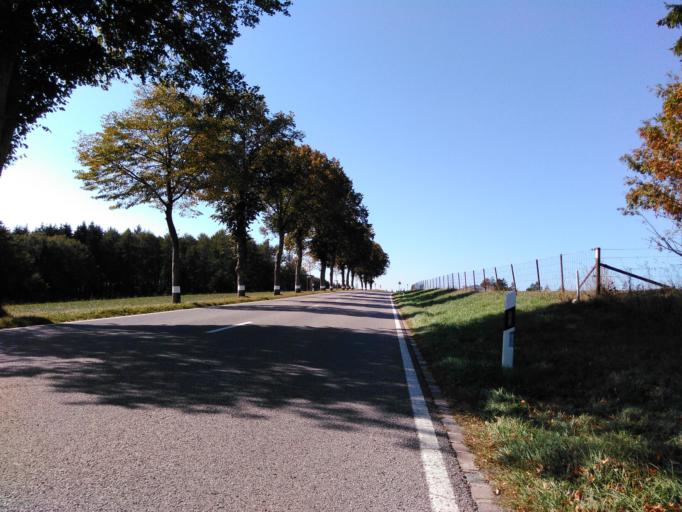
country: LU
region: Diekirch
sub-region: Canton de Redange
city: Rambrouch
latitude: 49.8394
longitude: 5.8309
